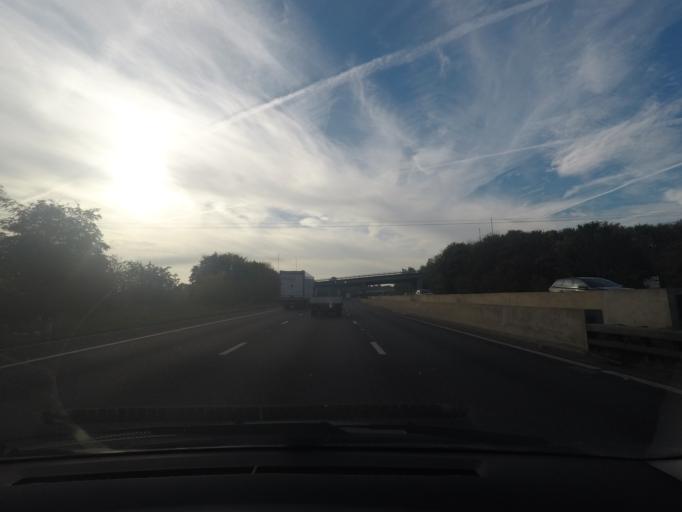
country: GB
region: England
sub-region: Barnsley
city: Darton
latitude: 53.5873
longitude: -1.5359
